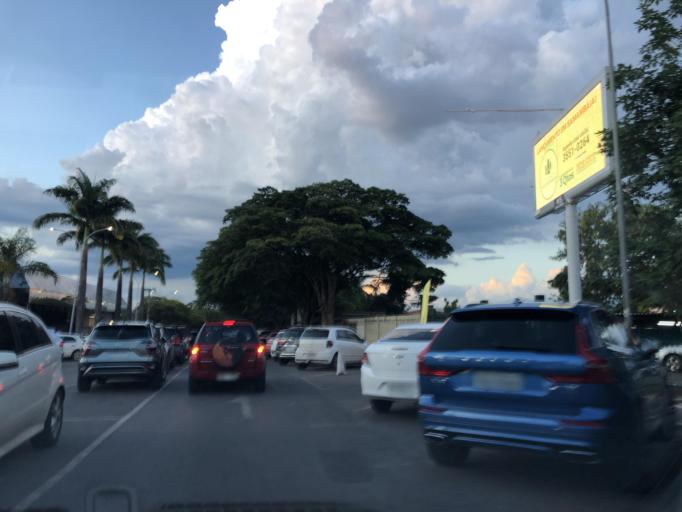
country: BR
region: Federal District
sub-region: Brasilia
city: Brasilia
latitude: -15.8465
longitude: -47.8936
